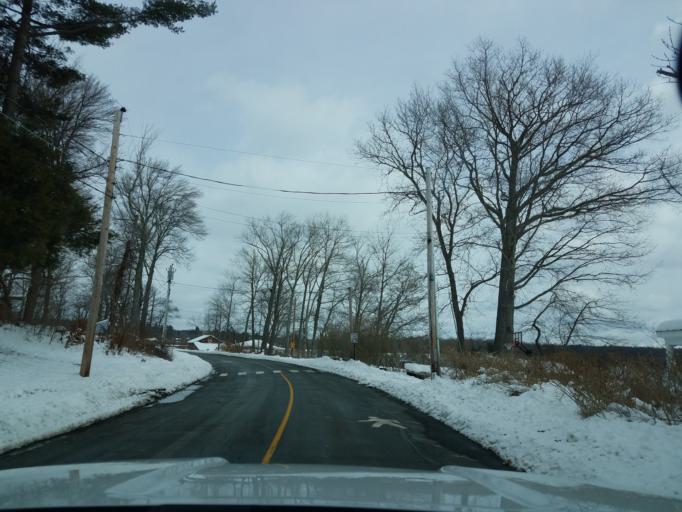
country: US
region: Connecticut
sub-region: Litchfield County
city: Litchfield
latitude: 41.7102
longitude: -73.2317
